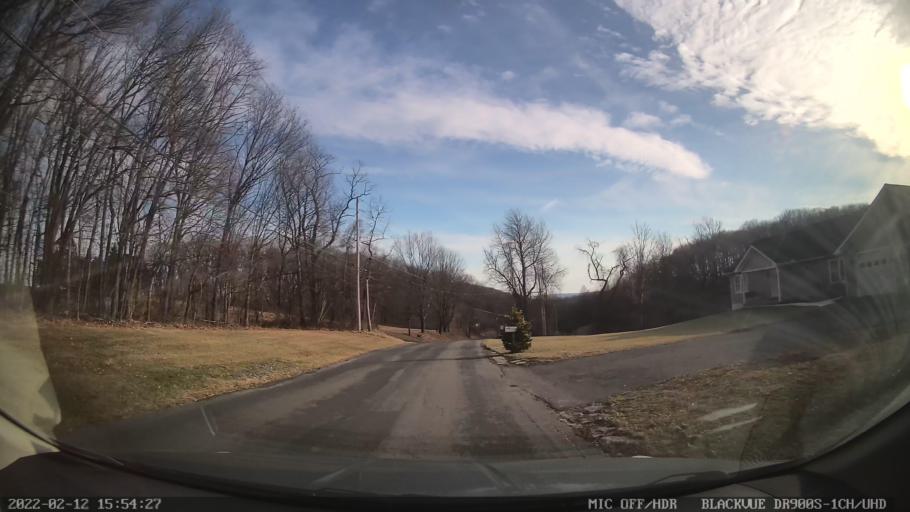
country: US
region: Pennsylvania
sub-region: Berks County
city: Kutztown
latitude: 40.5711
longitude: -75.7519
